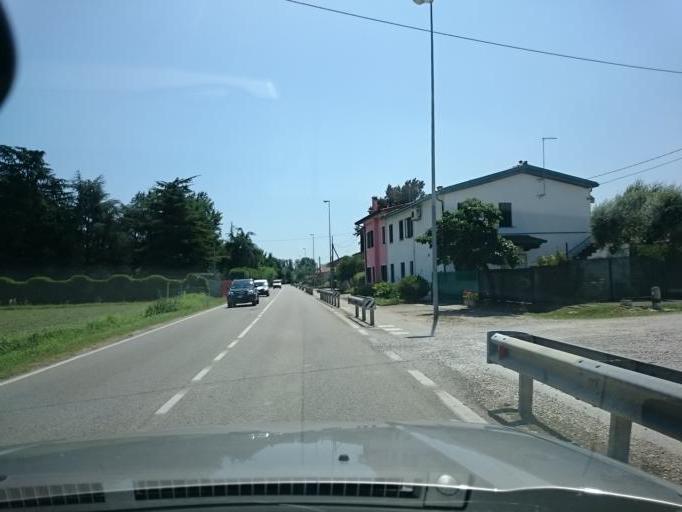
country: IT
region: Veneto
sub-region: Provincia di Padova
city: Villaguattera
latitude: 45.4372
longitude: 11.8234
